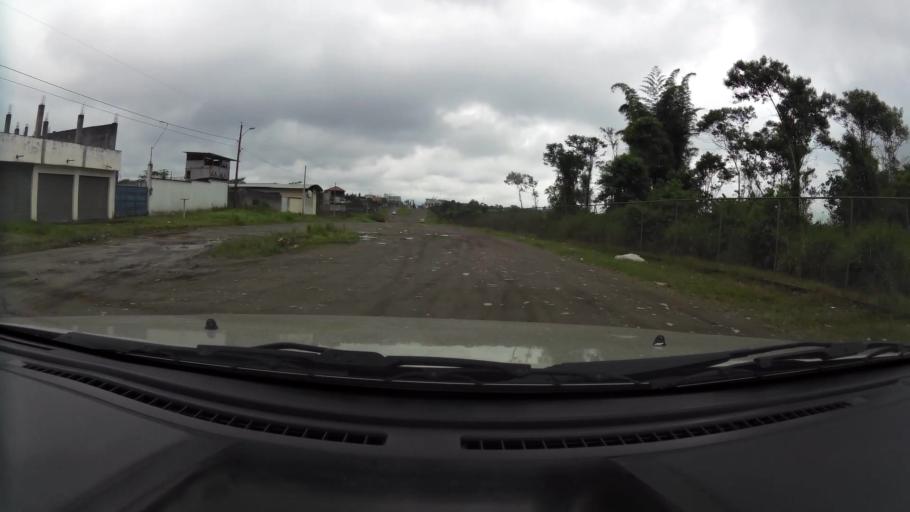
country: EC
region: Santo Domingo de los Tsachilas
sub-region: Canton Santo Domingo de los Colorados
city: Santo Domingo de los Colorados
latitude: -0.2412
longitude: -79.1603
